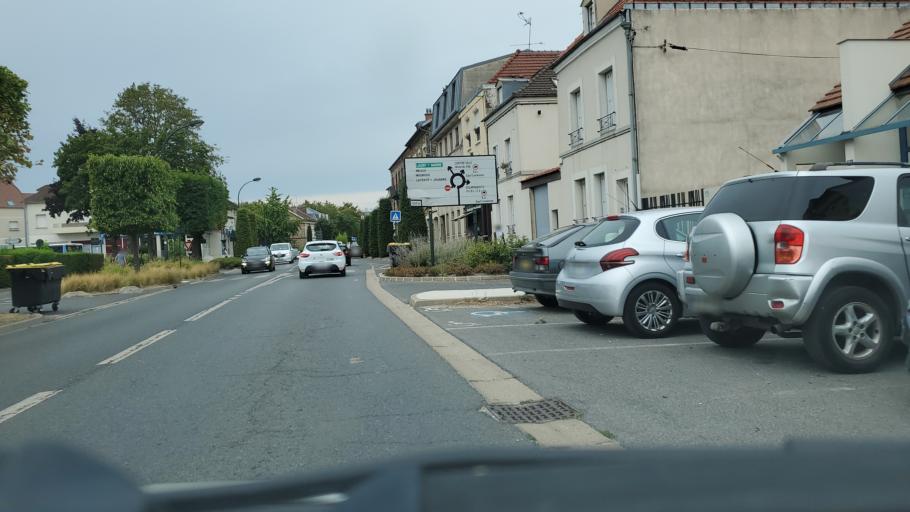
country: FR
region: Ile-de-France
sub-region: Departement de Seine-et-Marne
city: Coulommiers
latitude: 48.8074
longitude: 3.0835
